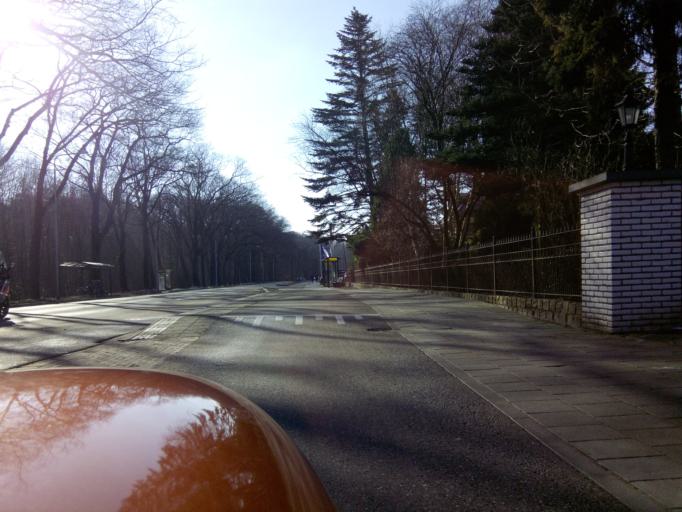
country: NL
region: Gelderland
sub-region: Gemeente Barneveld
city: Barneveld
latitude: 52.1521
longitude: 5.5959
